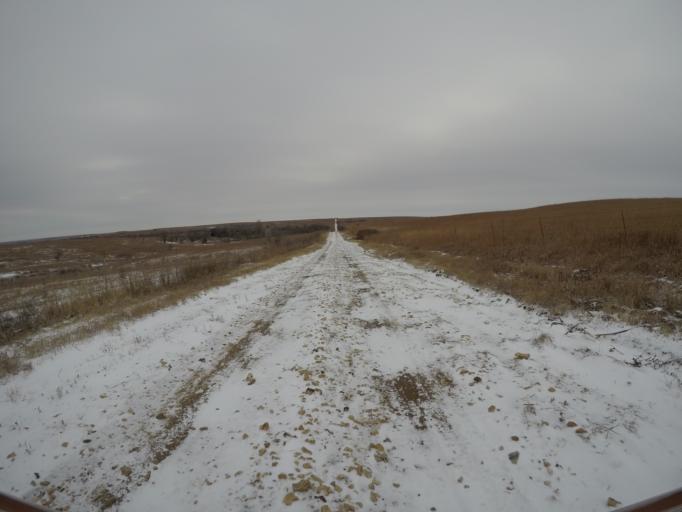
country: US
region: Kansas
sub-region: Wabaunsee County
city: Alma
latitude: 38.8716
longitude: -96.1136
